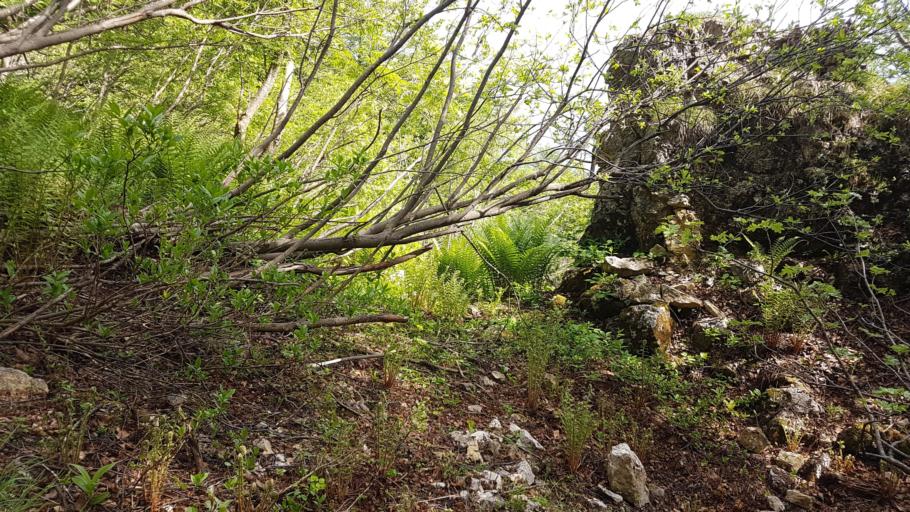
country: IT
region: Veneto
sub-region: Provincia di Vicenza
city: Recoaro Terme
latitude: 45.6724
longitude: 11.1959
